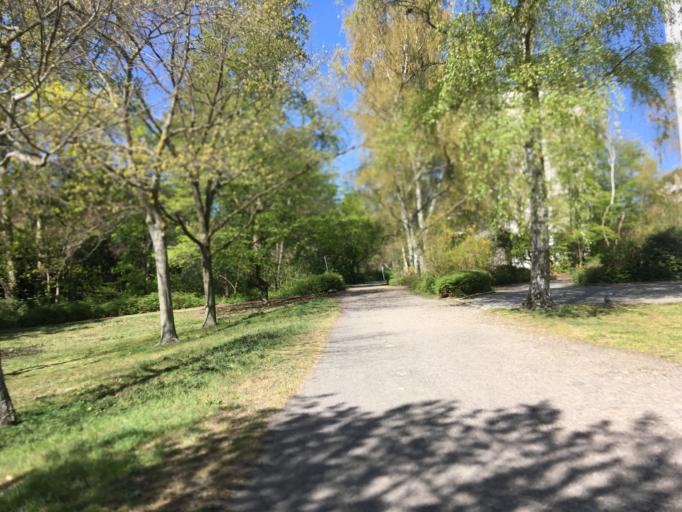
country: DE
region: Berlin
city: Reinickendorf
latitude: 52.5688
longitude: 13.3420
